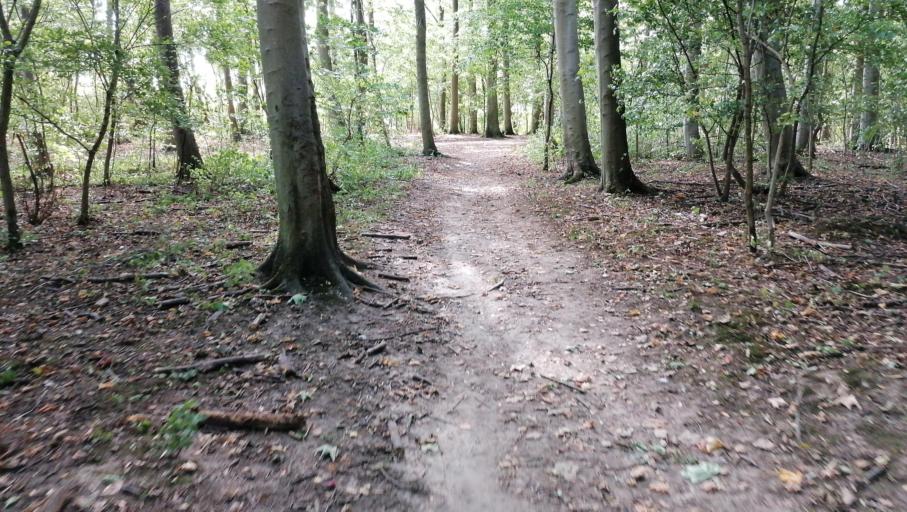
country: DK
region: Zealand
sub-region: Holbaek Kommune
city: Holbaek
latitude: 55.7134
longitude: 11.6961
